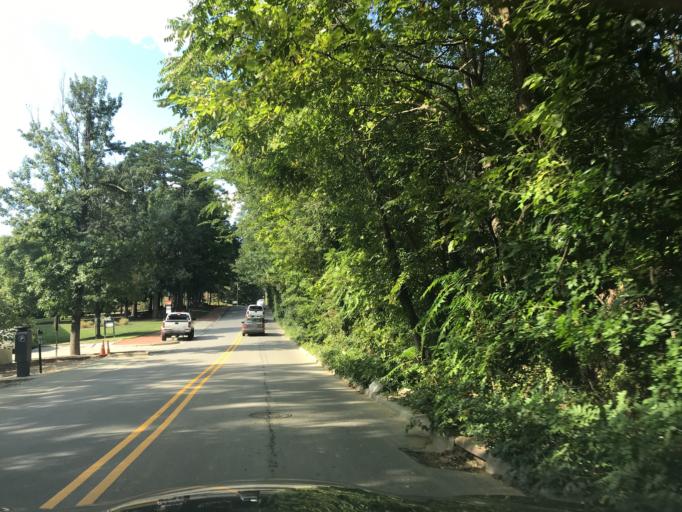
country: US
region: North Carolina
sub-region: Orange County
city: Chapel Hill
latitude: 35.9076
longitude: -79.0416
